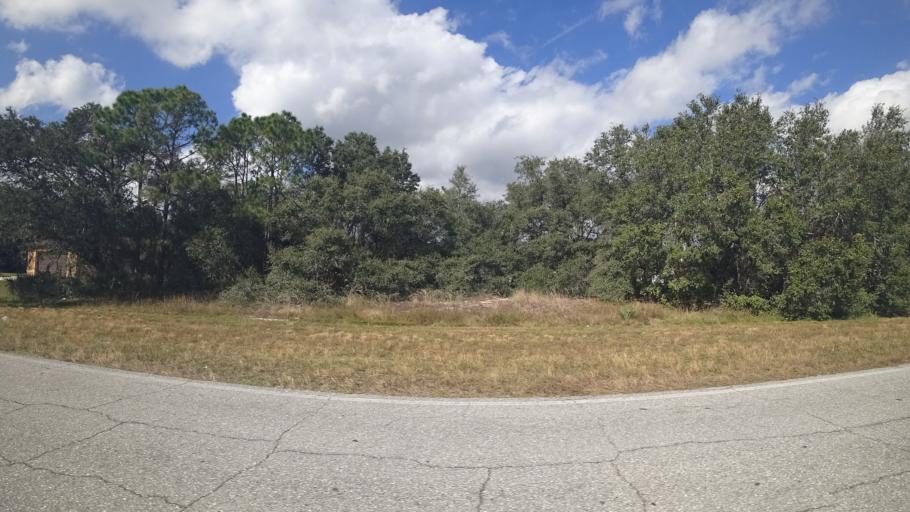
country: US
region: Florida
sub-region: Charlotte County
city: Port Charlotte
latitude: 27.0495
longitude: -82.1201
